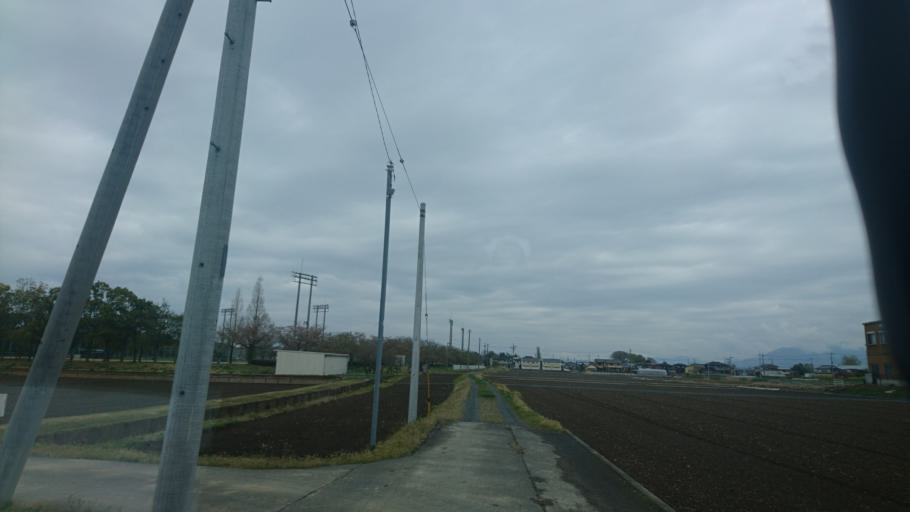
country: JP
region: Ibaraki
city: Ishige
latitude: 36.1509
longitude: 139.9615
